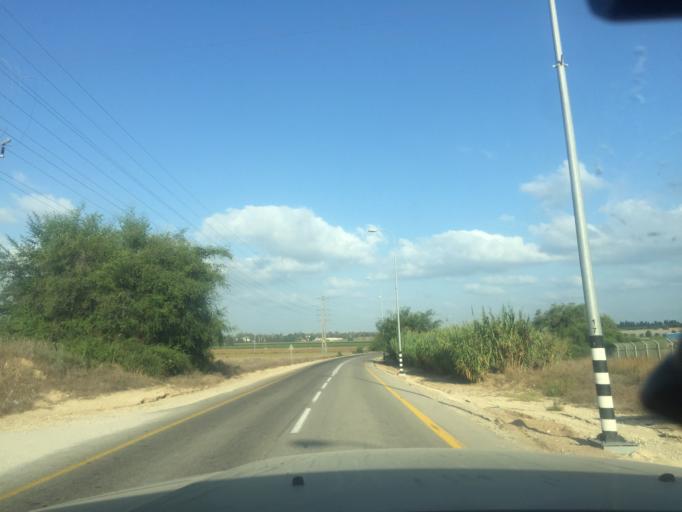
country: PS
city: Umm an Nasr
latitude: 31.6047
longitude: 34.5600
